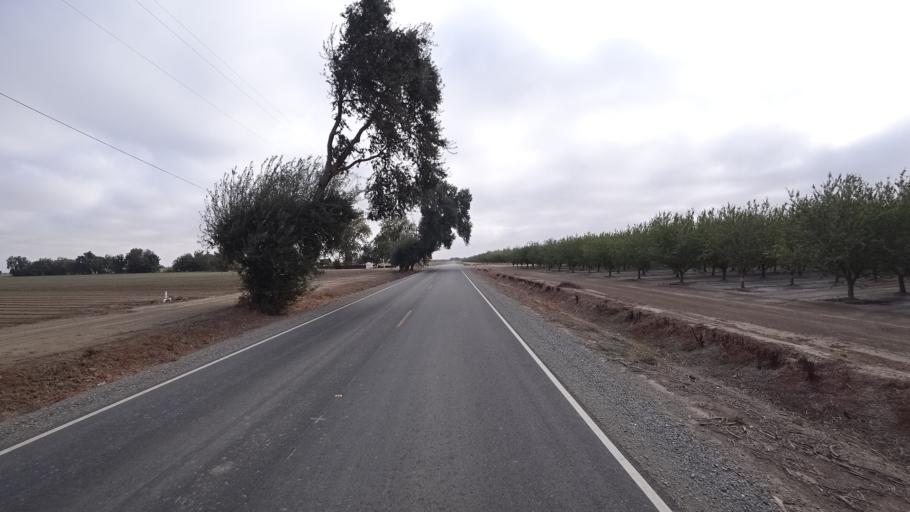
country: US
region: California
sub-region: Yolo County
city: Dunnigan
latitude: 38.7942
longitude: -121.8704
